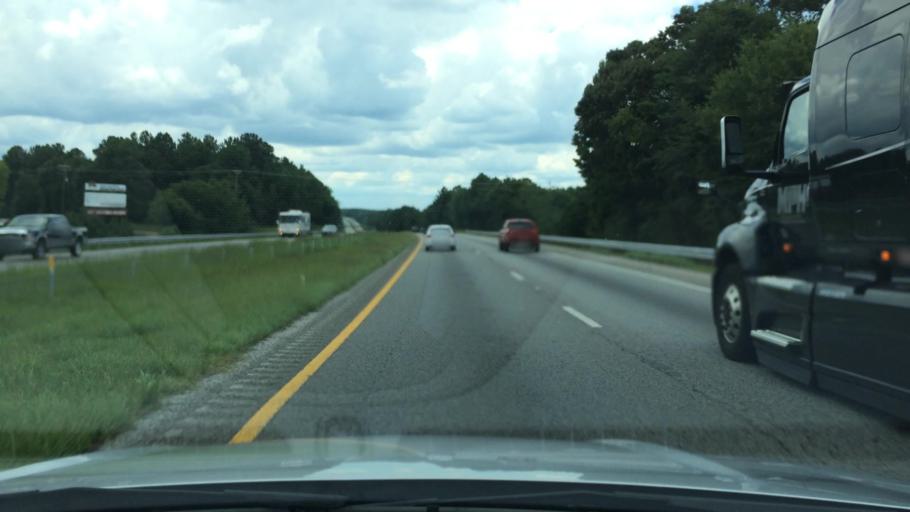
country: US
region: South Carolina
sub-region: Spartanburg County
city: Woodruff
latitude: 34.7761
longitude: -81.9535
